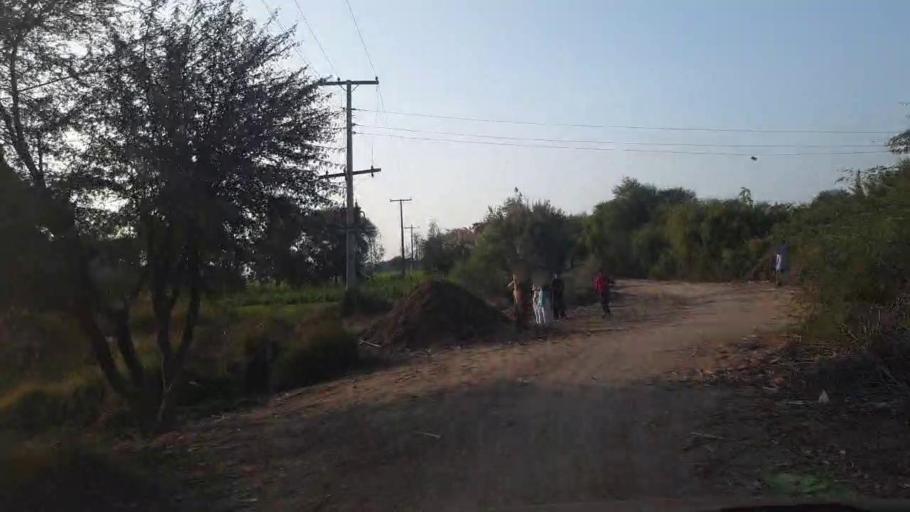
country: PK
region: Sindh
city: Berani
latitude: 25.8615
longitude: 68.7336
